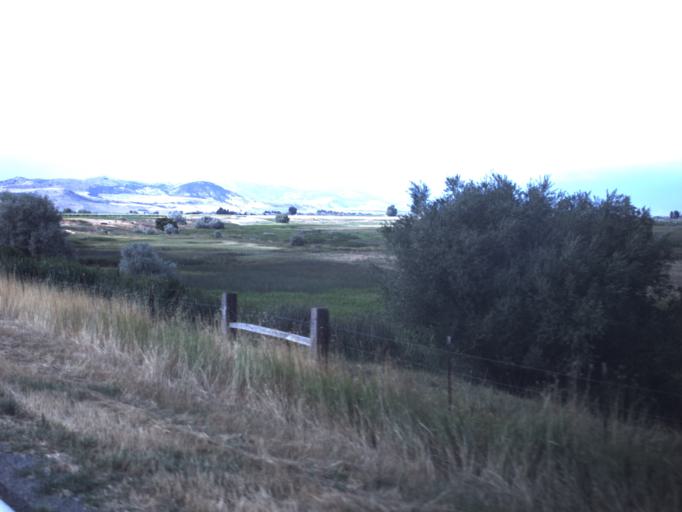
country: US
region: Utah
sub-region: Cache County
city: Lewiston
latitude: 41.9148
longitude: -111.9302
